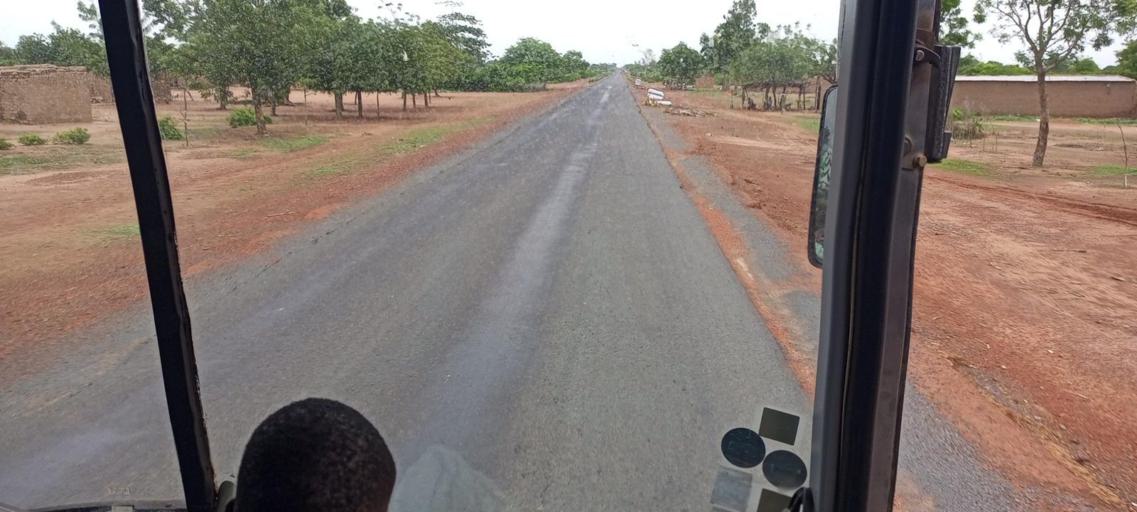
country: ML
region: Sikasso
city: Koutiala
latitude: 12.5455
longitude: -5.5797
